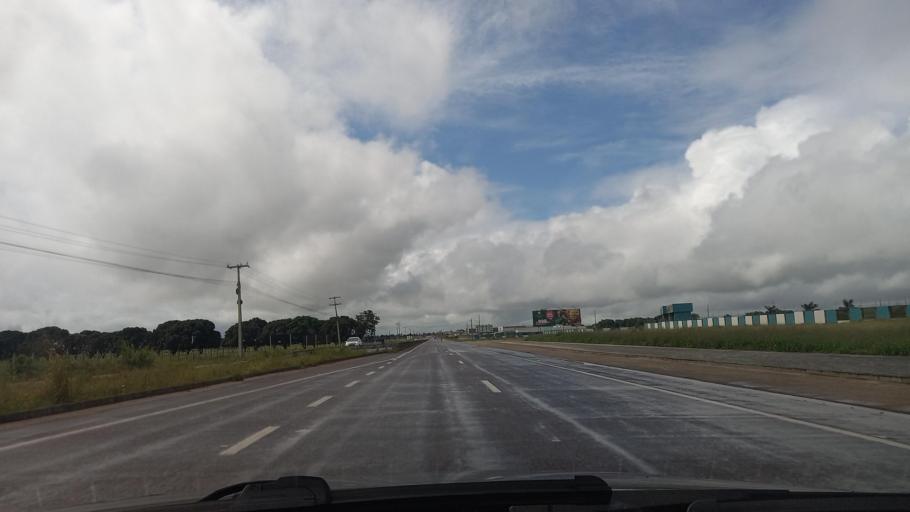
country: BR
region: Alagoas
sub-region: Limoeiro De Anadia
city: Limoeiro de Anadia
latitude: -9.7586
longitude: -36.5510
